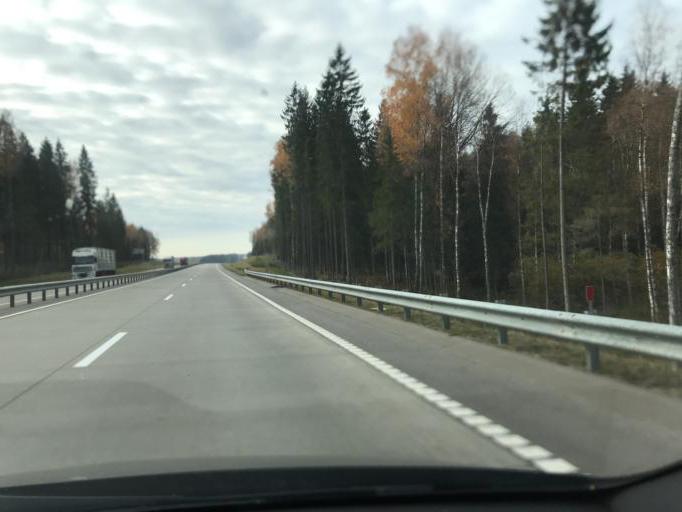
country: BY
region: Minsk
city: Rakaw
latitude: 54.0145
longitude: 27.1367
